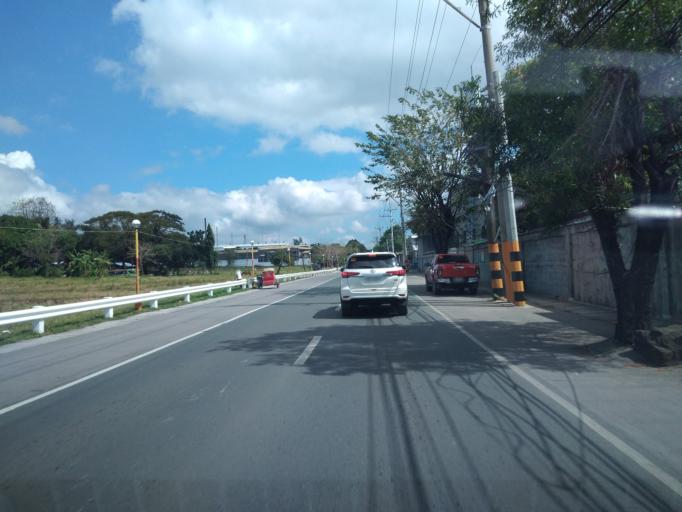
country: PH
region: Central Luzon
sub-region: Province of Bulacan
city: Guyong
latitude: 14.8282
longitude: 120.9713
